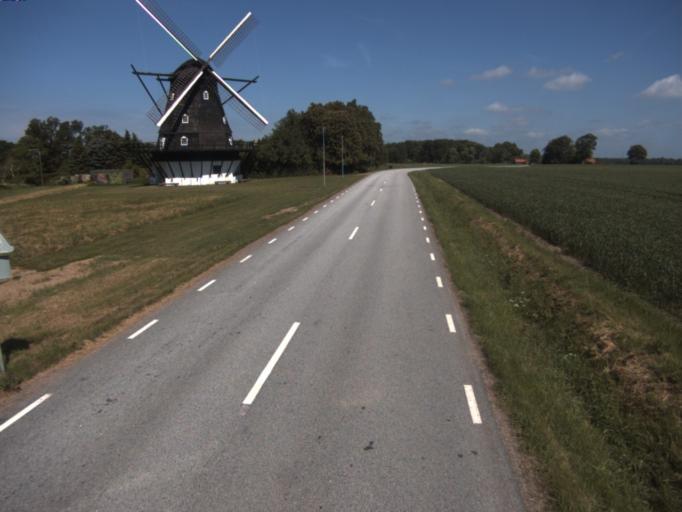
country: DK
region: Capital Region
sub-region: Helsingor Kommune
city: Helsingor
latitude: 56.1029
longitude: 12.6388
